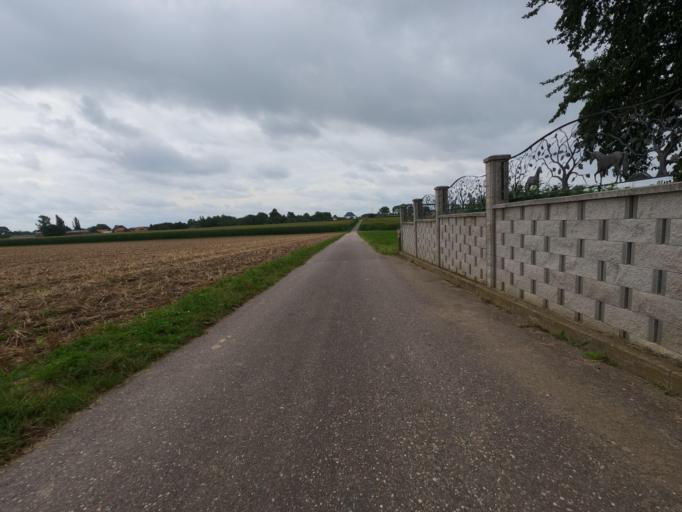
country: DE
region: North Rhine-Westphalia
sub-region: Regierungsbezirk Koln
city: Selfkant
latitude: 51.0214
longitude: 5.9573
